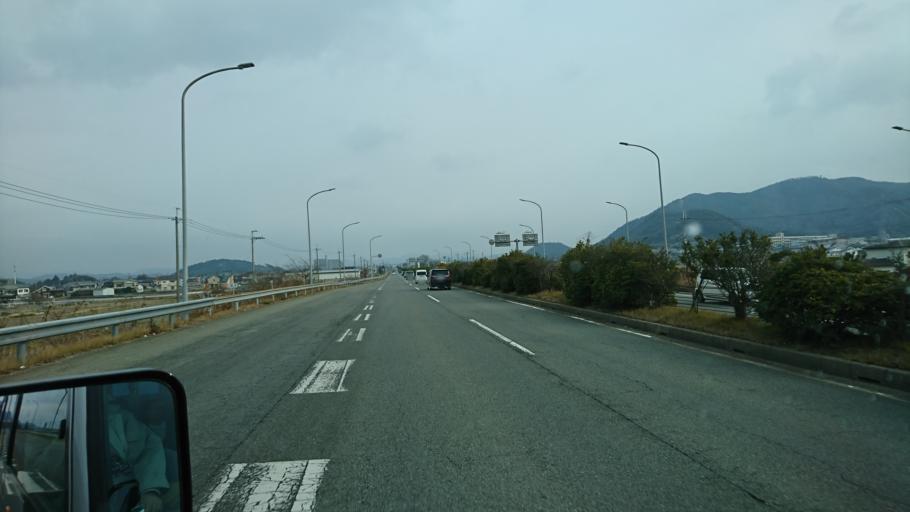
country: JP
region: Hyogo
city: Himeji
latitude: 34.8781
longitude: 134.7394
